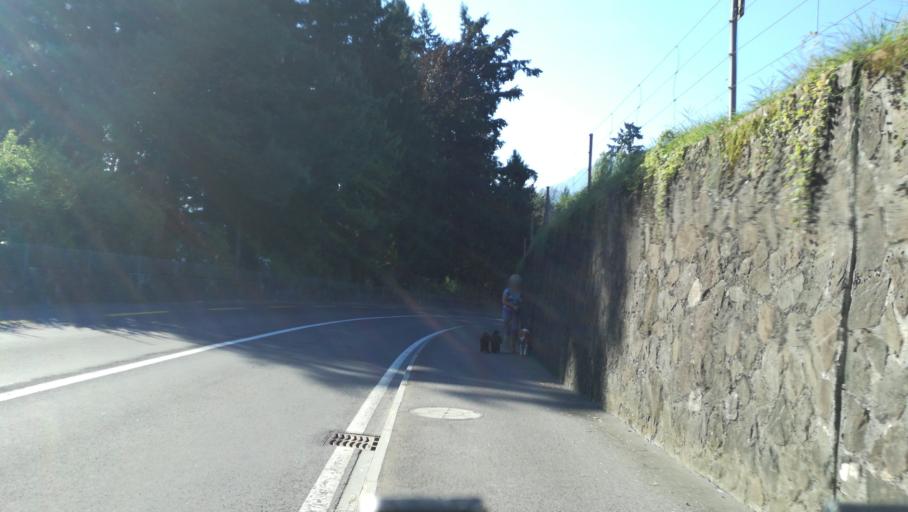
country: CH
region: Lucerne
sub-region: Lucerne-Land District
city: Meierskappel
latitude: 47.1195
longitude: 8.4628
